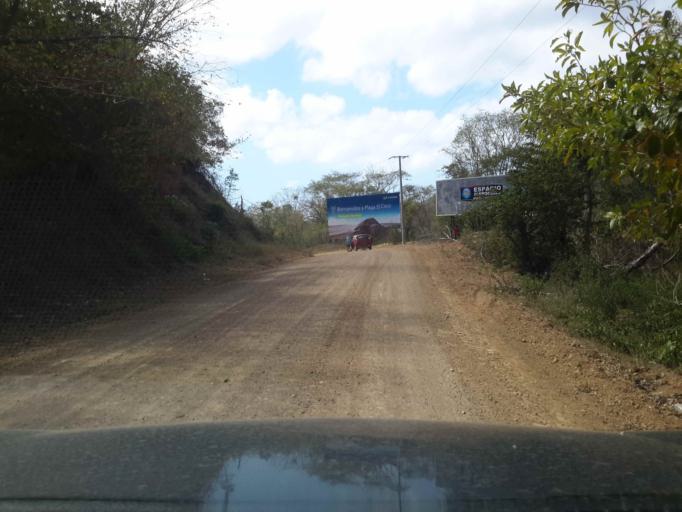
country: NI
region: Rivas
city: San Juan del Sur
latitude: 11.1686
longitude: -85.7971
